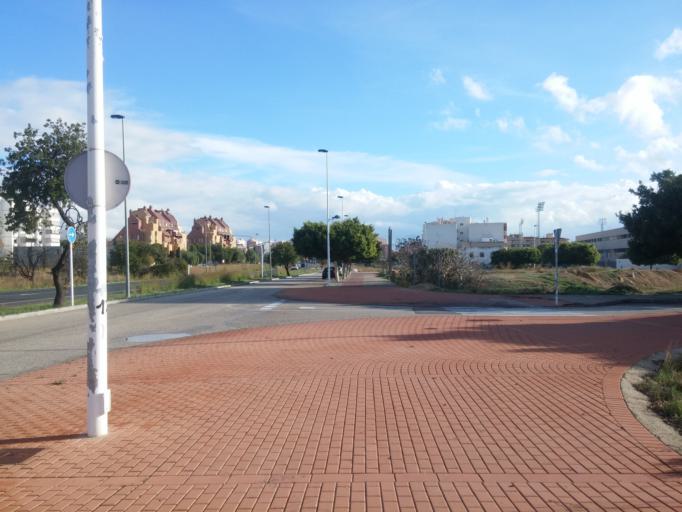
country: ES
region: Valencia
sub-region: Provincia de Alicante
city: Villajoyosa
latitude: 38.5023
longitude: -0.2433
